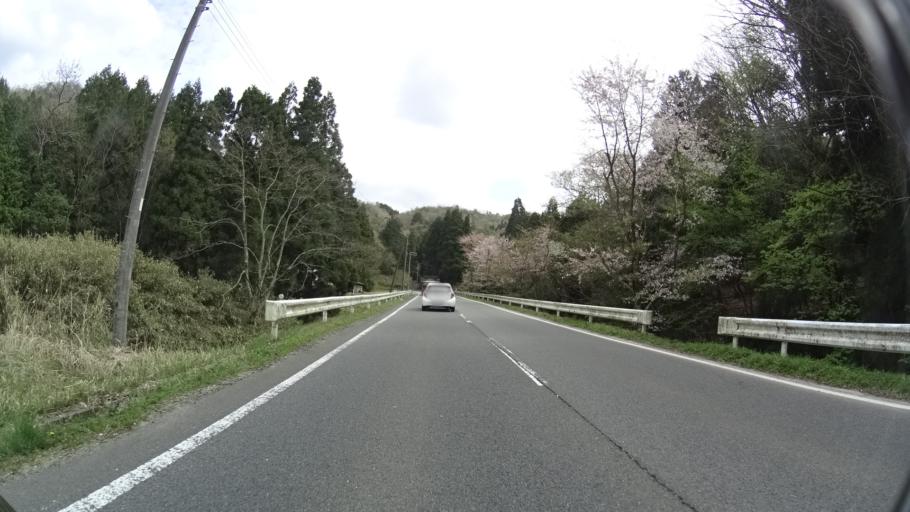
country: JP
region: Hyogo
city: Toyooka
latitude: 35.5058
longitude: 134.8630
